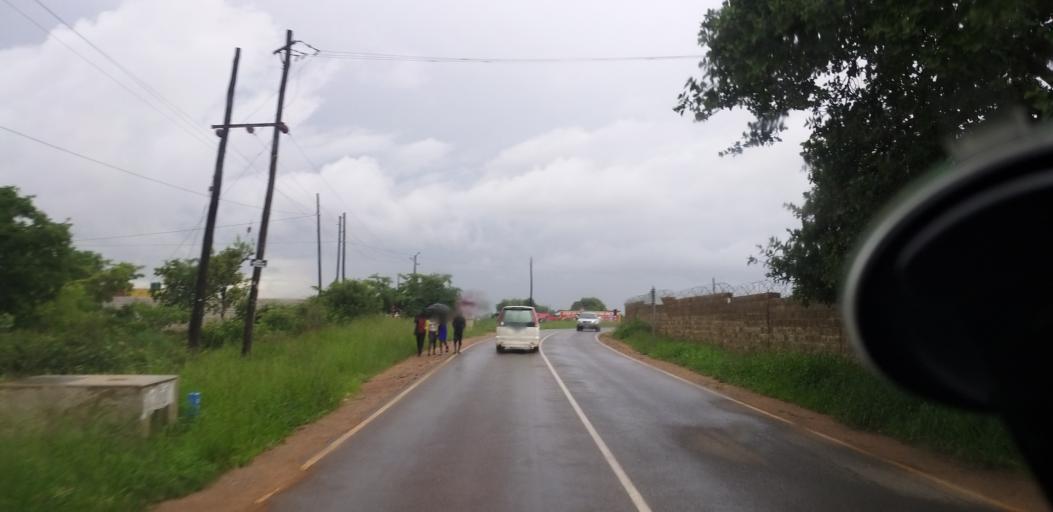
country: ZM
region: Lusaka
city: Lusaka
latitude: -15.4897
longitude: 28.3141
